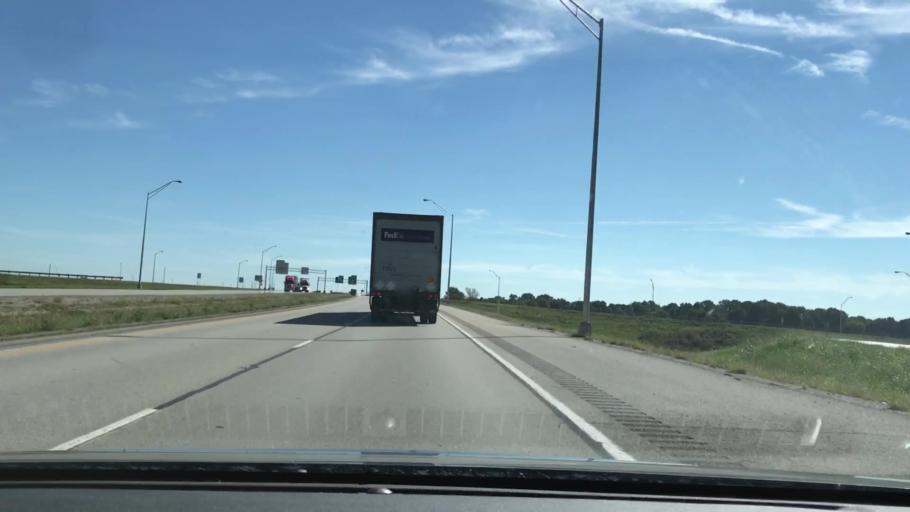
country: US
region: Kentucky
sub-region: Warren County
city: Plano
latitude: 36.9116
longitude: -86.4358
